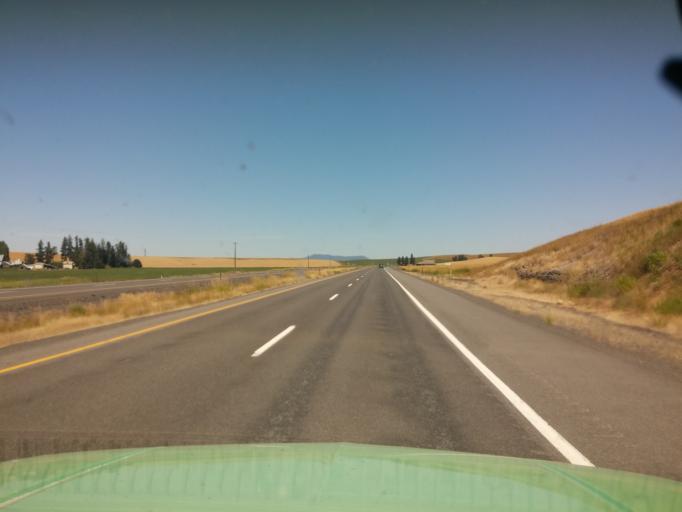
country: US
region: Idaho
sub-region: Nez Perce County
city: Lewiston
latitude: 46.5710
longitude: -116.9481
